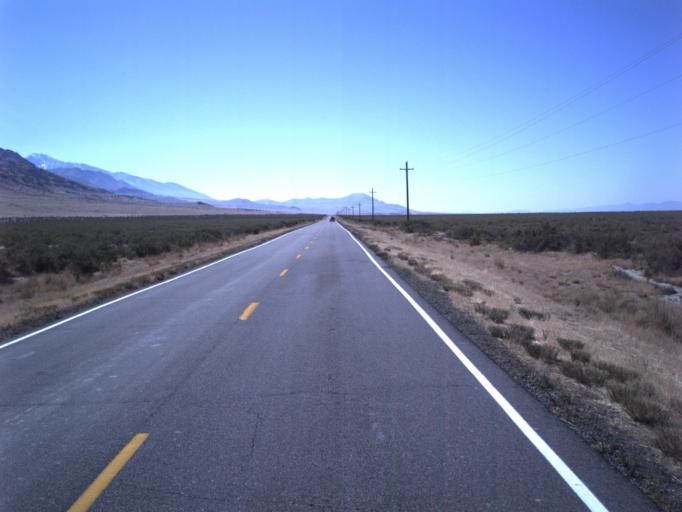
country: US
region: Utah
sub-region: Tooele County
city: Grantsville
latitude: 40.7187
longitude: -112.6608
